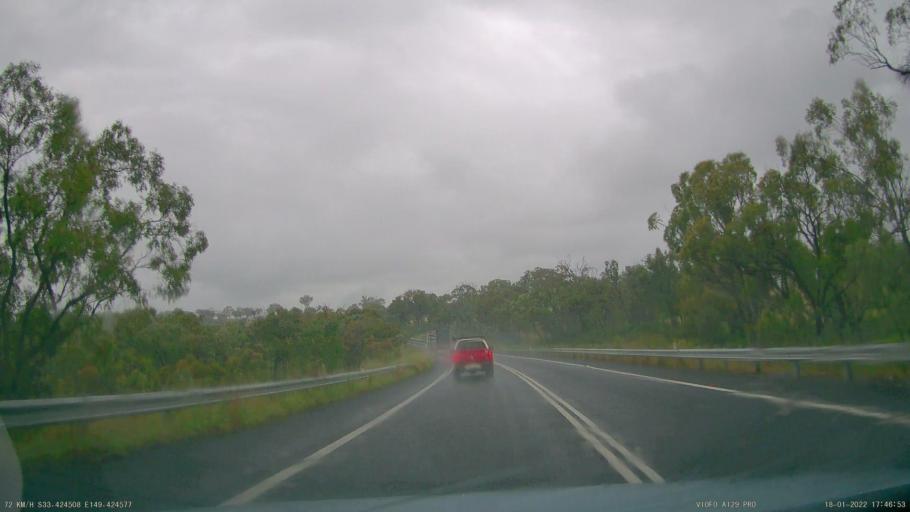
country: AU
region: New South Wales
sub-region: Bathurst Regional
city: Eglinton
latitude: -33.4244
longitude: 149.4247
